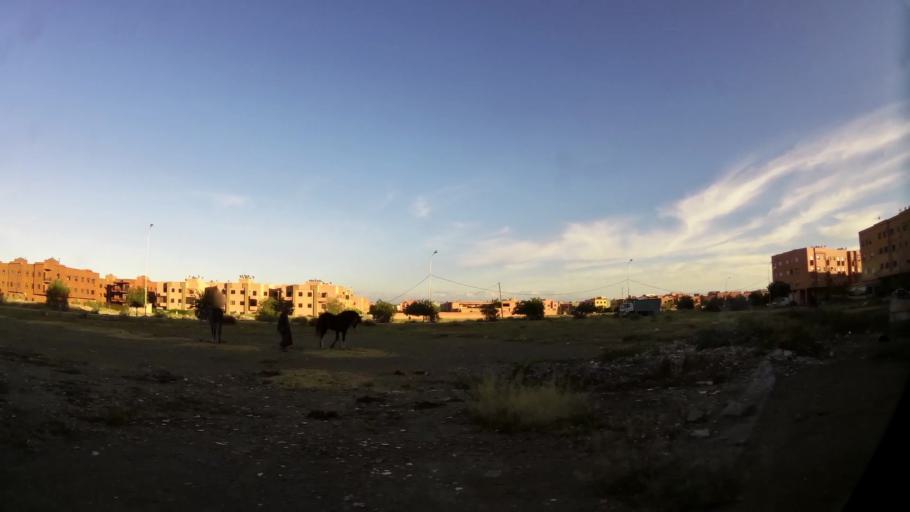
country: MA
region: Marrakech-Tensift-Al Haouz
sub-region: Marrakech
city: Marrakesh
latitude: 31.7495
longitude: -8.1112
